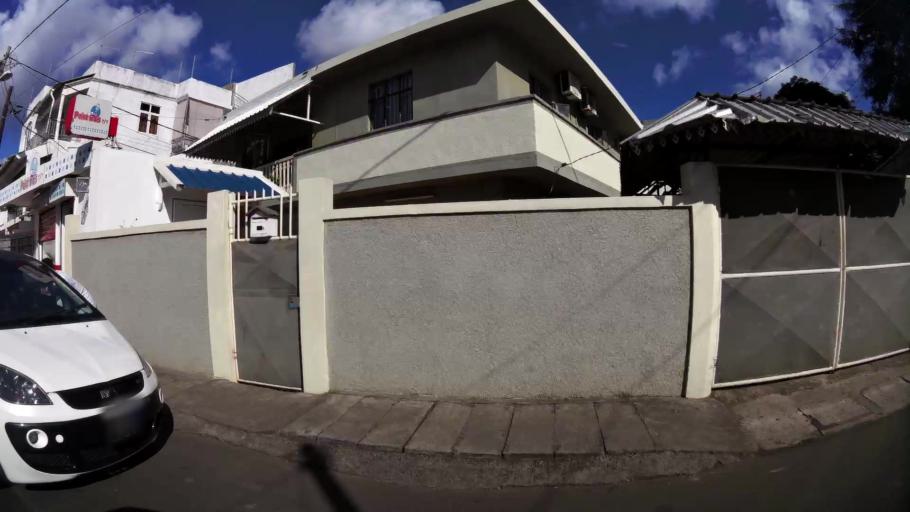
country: MU
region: Pamplemousses
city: Le Hochet
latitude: -20.1471
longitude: 57.5198
